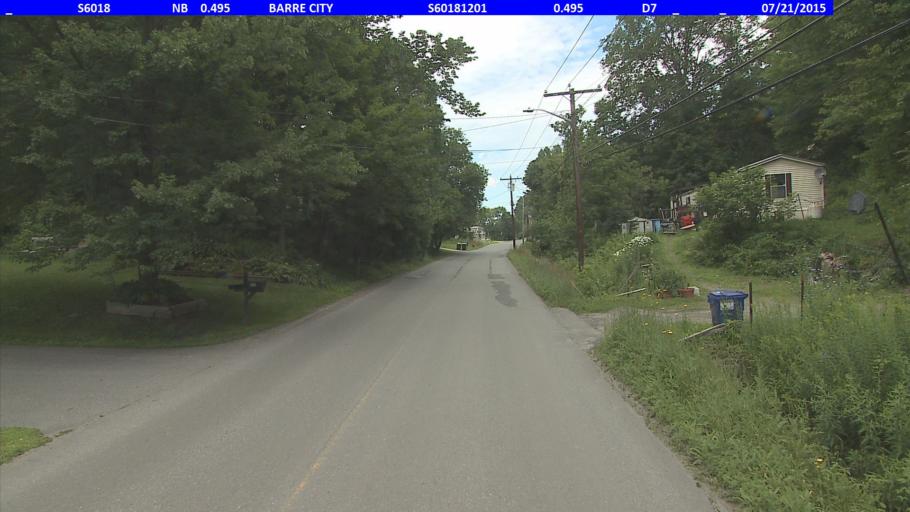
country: US
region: Vermont
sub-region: Washington County
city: Barre
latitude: 44.2061
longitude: -72.5003
